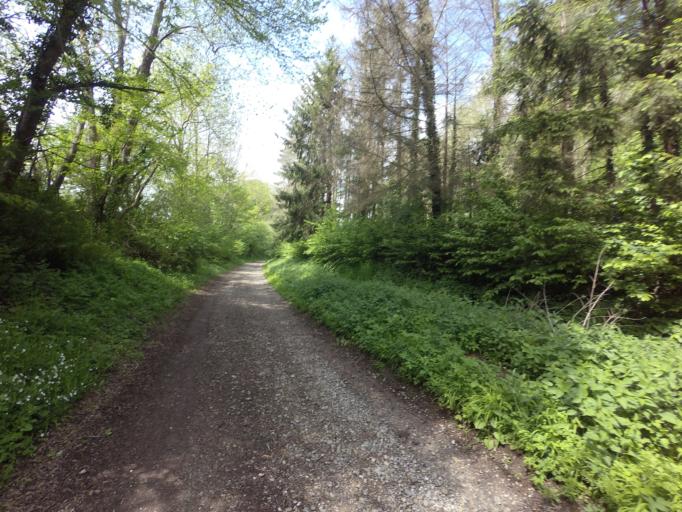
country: NL
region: Limburg
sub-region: Gemeente Maastricht
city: Heer
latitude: 50.8219
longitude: 5.7675
